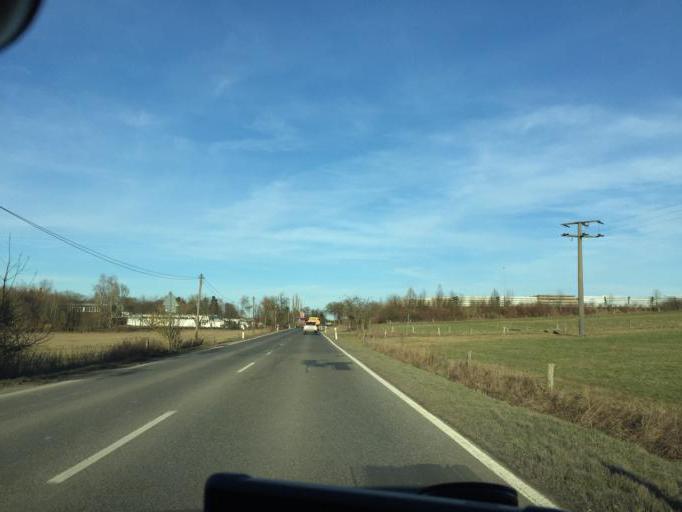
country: DE
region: Rheinland-Pfalz
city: Ruppach-Goldhausen
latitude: 50.4849
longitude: 7.8878
